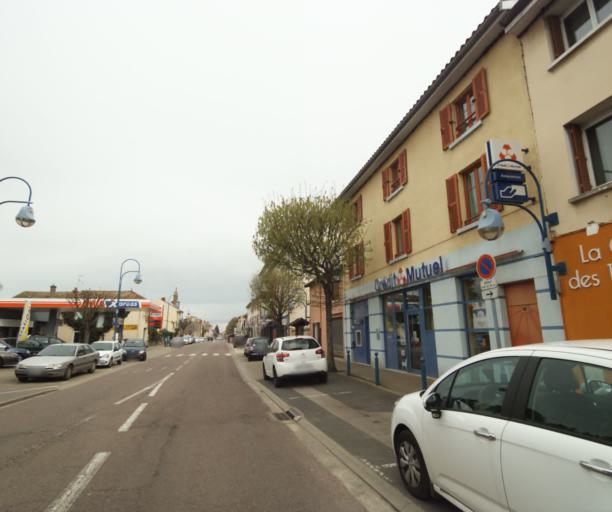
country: FR
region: Bourgogne
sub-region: Departement de Saone-et-Loire
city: Charnay-les-Macon
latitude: 46.3086
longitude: 4.8096
